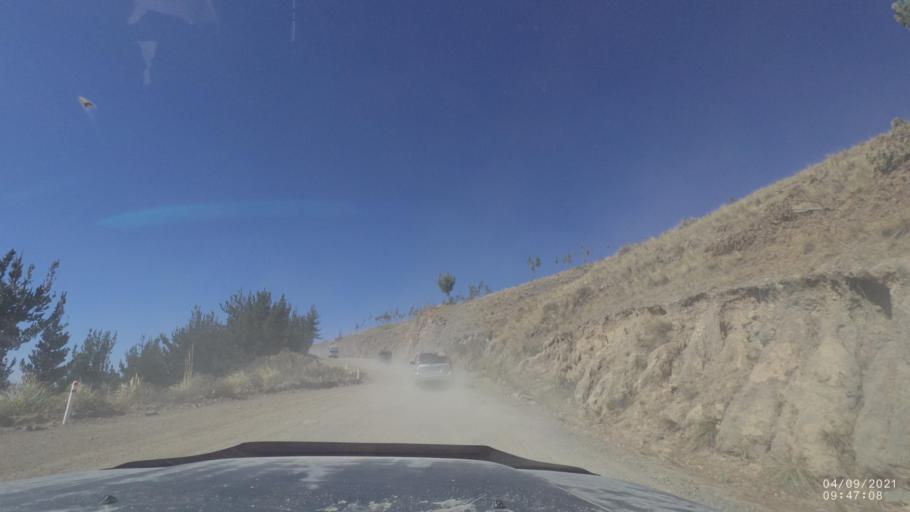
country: BO
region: Cochabamba
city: Sipe Sipe
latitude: -17.3529
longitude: -66.3875
